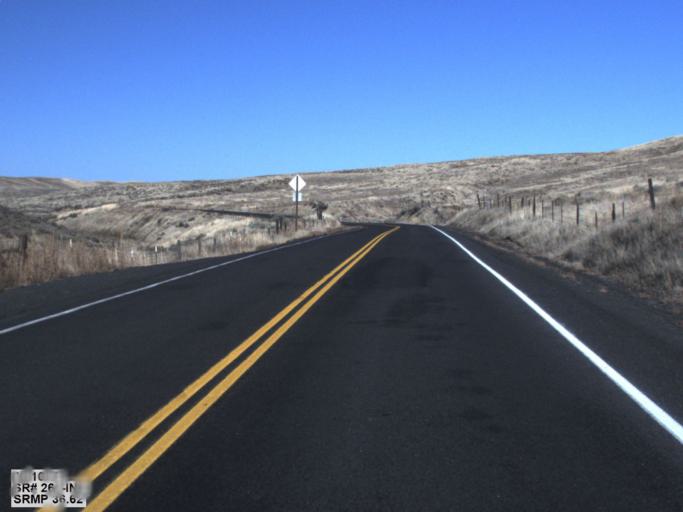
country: US
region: Washington
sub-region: Adams County
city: Ritzville
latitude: 46.7632
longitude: -118.2945
